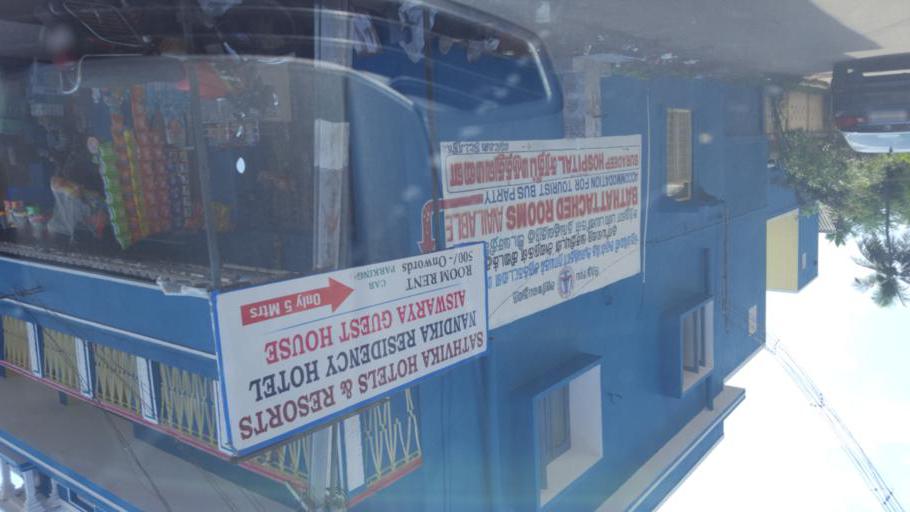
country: IN
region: Tamil Nadu
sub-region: Kancheepuram
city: Mamallapuram
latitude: 12.6180
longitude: 80.1941
